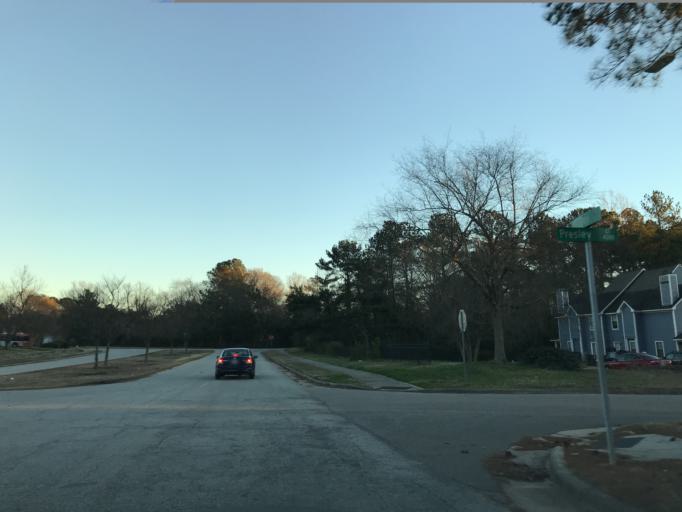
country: US
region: North Carolina
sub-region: Wake County
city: Raleigh
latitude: 35.8443
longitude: -78.5902
